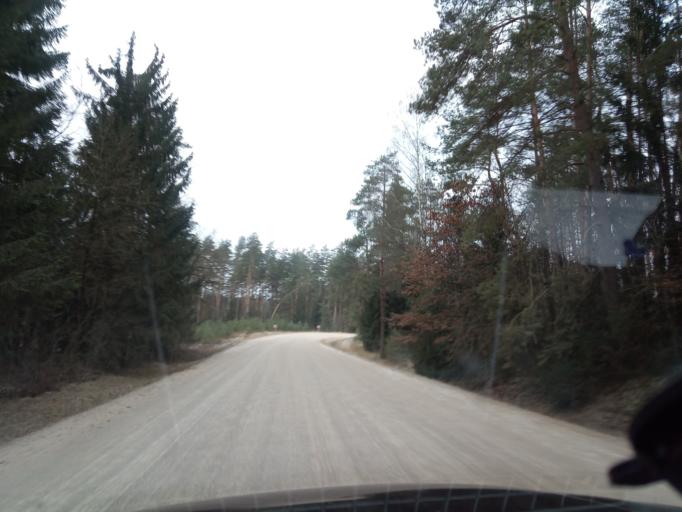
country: LT
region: Alytaus apskritis
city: Varena
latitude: 54.1483
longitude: 24.6022
